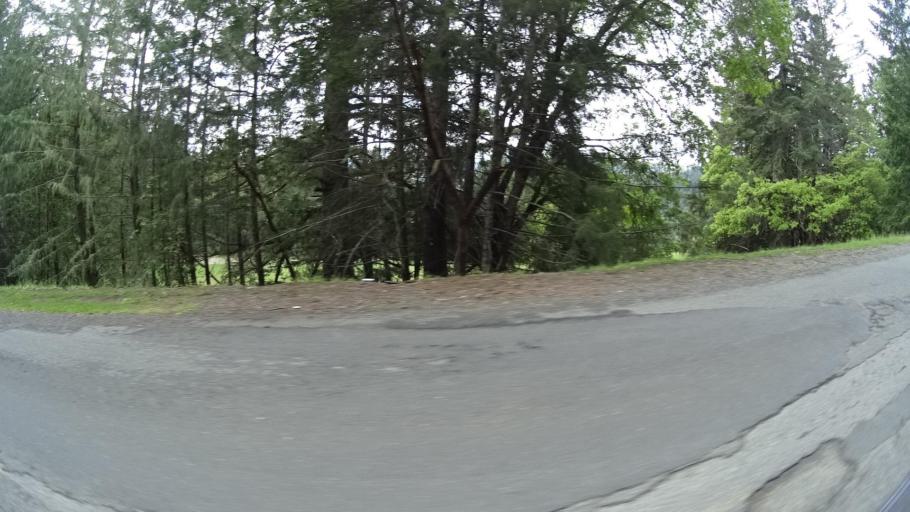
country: US
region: California
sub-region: Humboldt County
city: Redway
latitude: 40.1203
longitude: -123.6441
